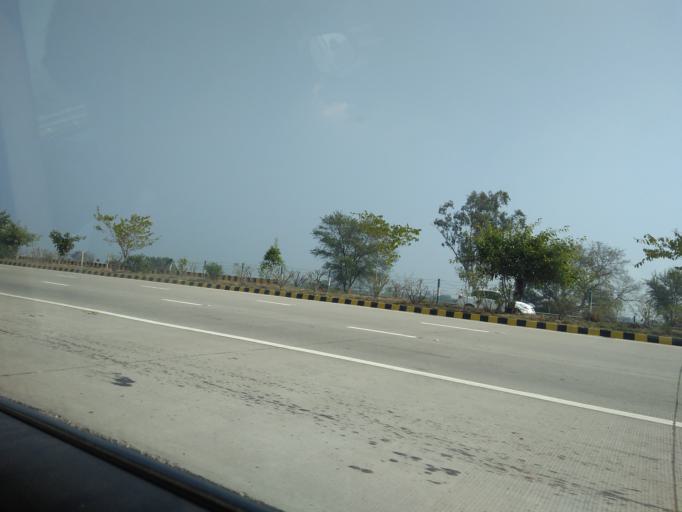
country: IN
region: Uttar Pradesh
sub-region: Mathura
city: Vrindavan
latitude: 27.6140
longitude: 77.7422
